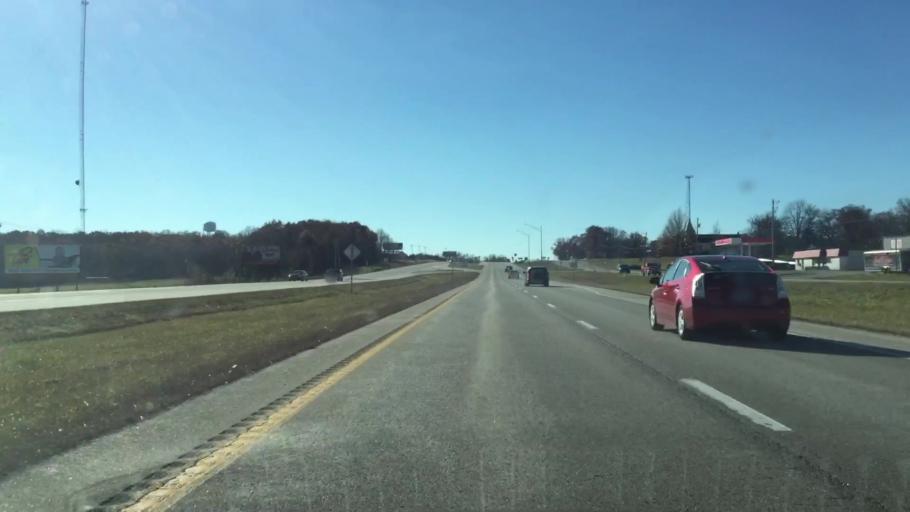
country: US
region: Missouri
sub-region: Cole County
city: Wardsville
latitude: 38.4478
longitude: -92.3027
